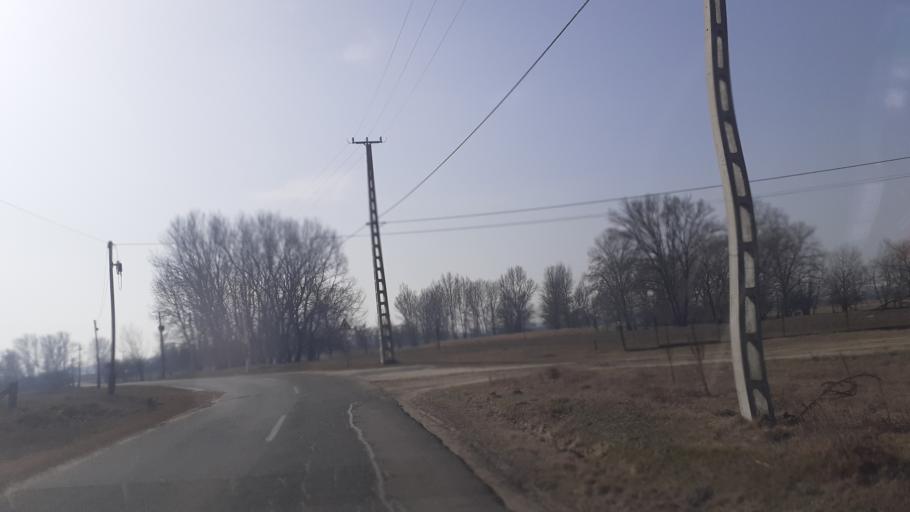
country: HU
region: Pest
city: Orkeny
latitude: 47.0779
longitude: 19.3641
